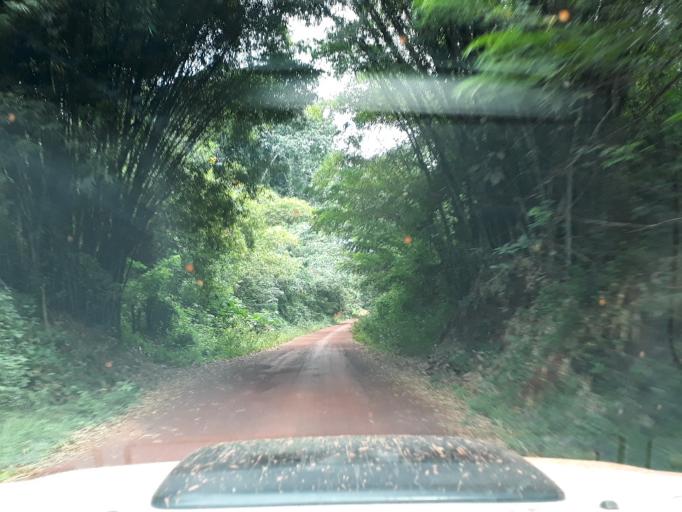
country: CD
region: Eastern Province
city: Buta
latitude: 2.4955
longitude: 24.8425
